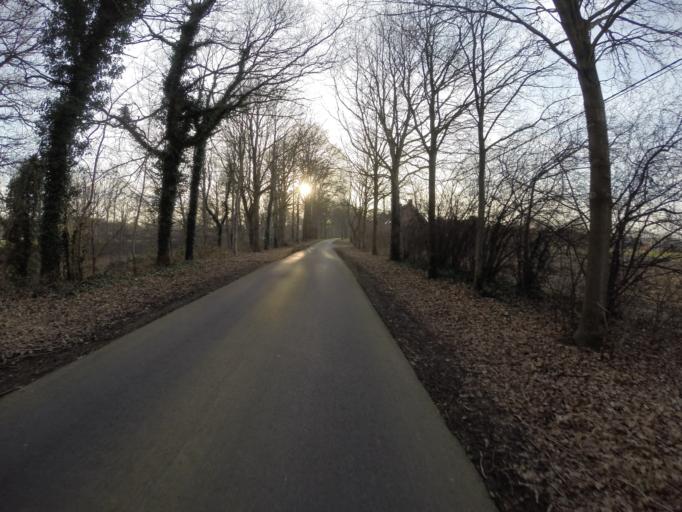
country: BE
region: Flanders
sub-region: Provincie Oost-Vlaanderen
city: Aalter
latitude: 51.1015
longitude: 3.4191
